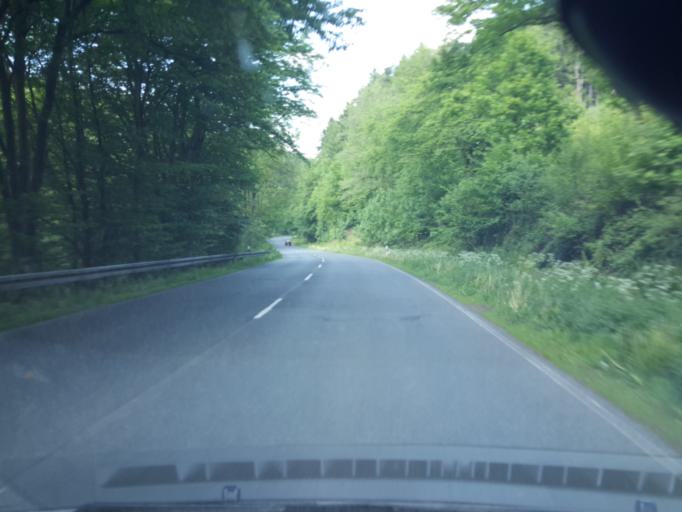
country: DE
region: North Rhine-Westphalia
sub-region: Regierungsbezirk Arnsberg
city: Hagen
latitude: 51.3206
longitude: 7.4561
